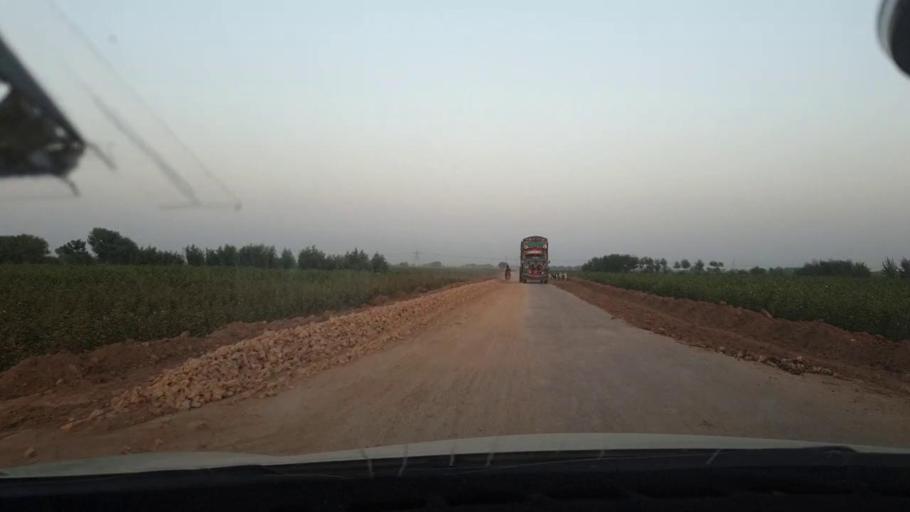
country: PK
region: Sindh
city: Bhit Shah
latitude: 25.7528
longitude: 68.5240
